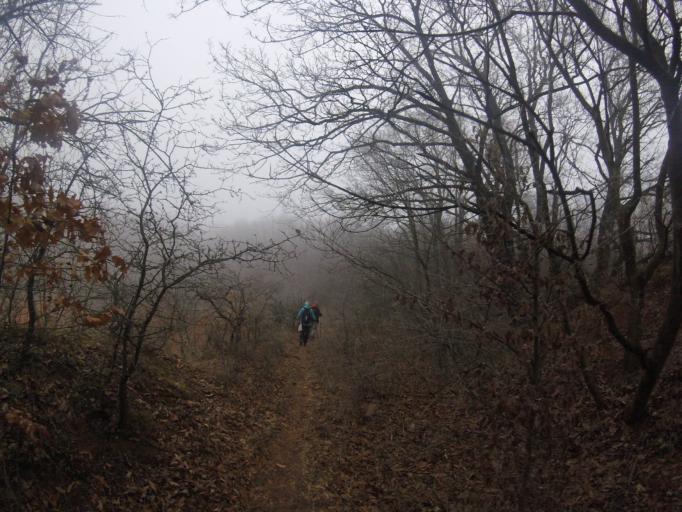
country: HU
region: Fejer
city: Zamoly
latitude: 47.3725
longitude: 18.3901
